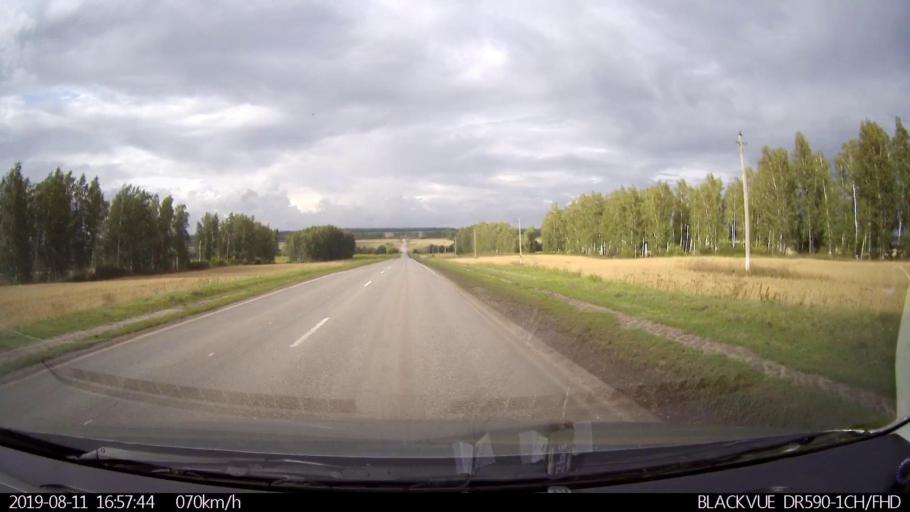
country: RU
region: Ulyanovsk
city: Mayna
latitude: 54.3001
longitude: 47.6514
